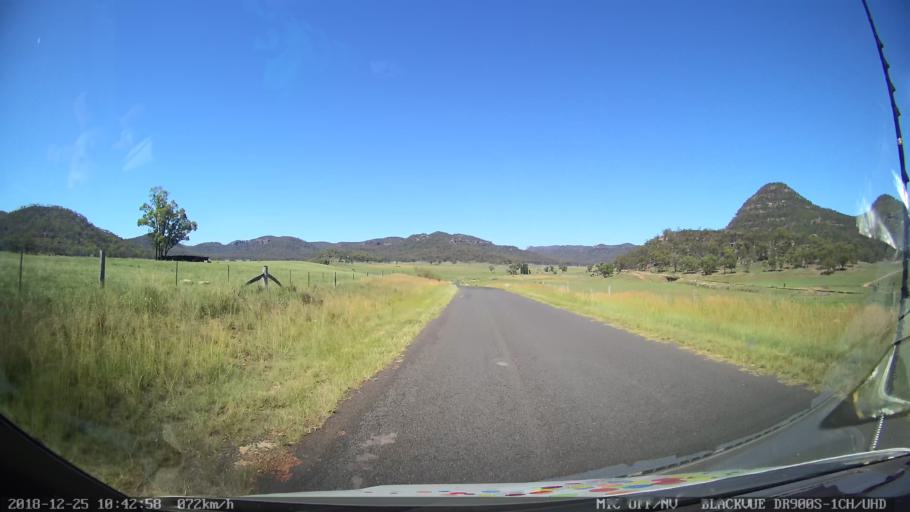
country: AU
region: New South Wales
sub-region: Upper Hunter Shire
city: Merriwa
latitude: -32.4192
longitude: 150.3178
